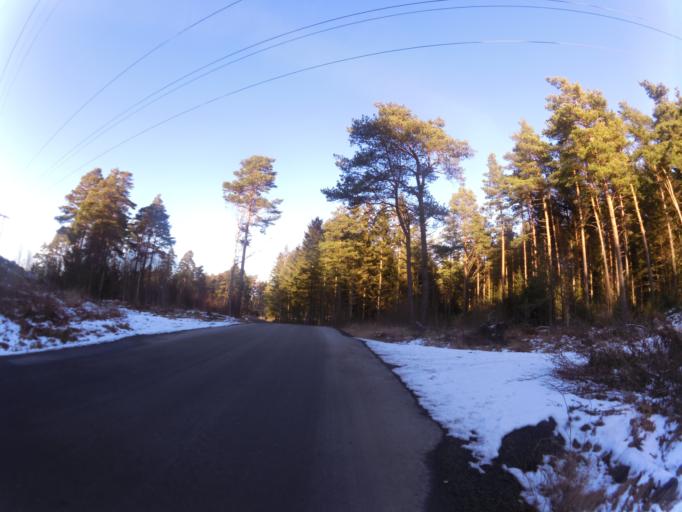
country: NO
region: Ostfold
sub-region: Fredrikstad
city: Lervik
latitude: 59.2597
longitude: 10.8061
